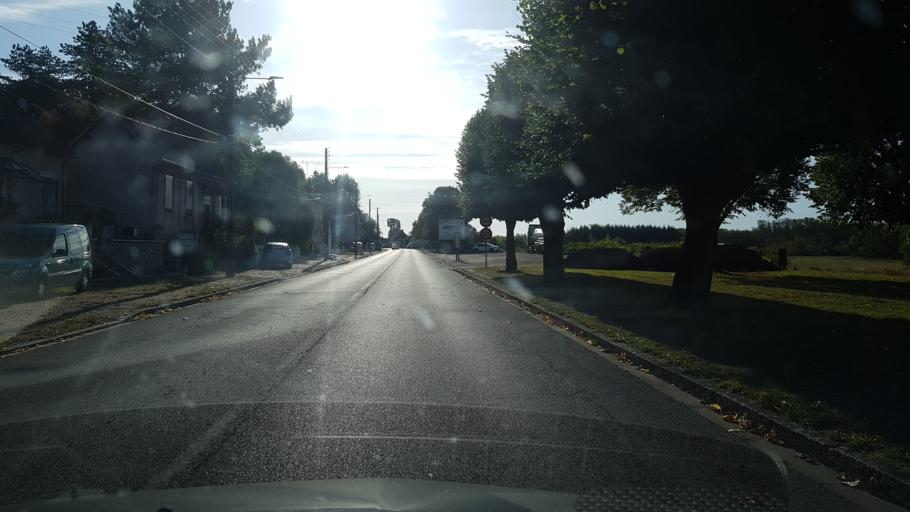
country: FR
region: Centre
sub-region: Departement du Loiret
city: Gien
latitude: 47.6787
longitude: 2.6466
